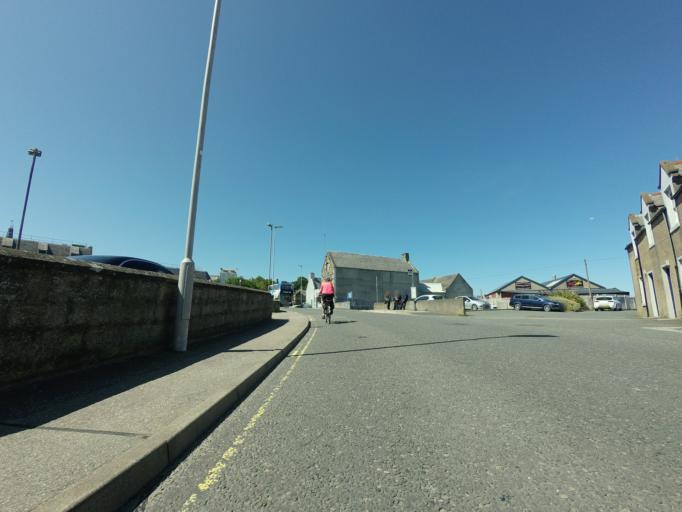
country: GB
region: Scotland
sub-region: Aberdeenshire
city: Banff
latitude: 57.6649
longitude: -2.5186
